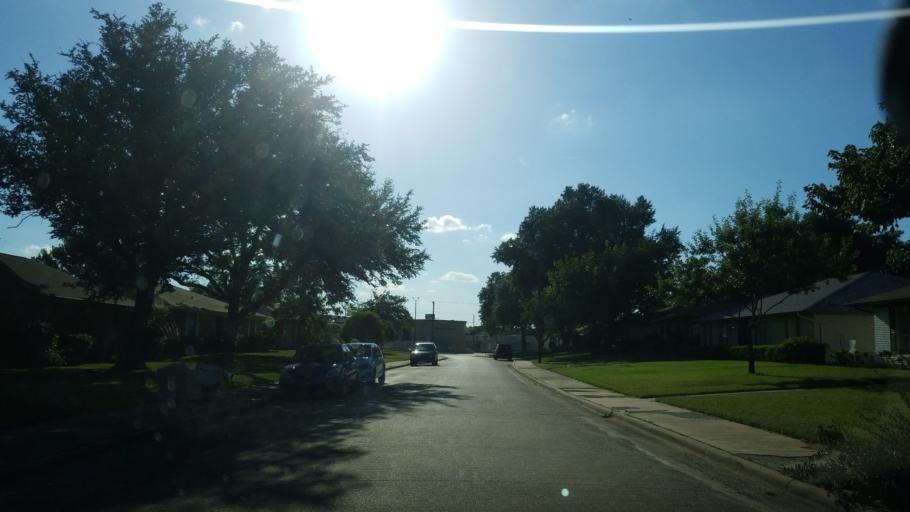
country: US
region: Texas
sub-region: Dallas County
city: Balch Springs
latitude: 32.7848
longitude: -96.7045
